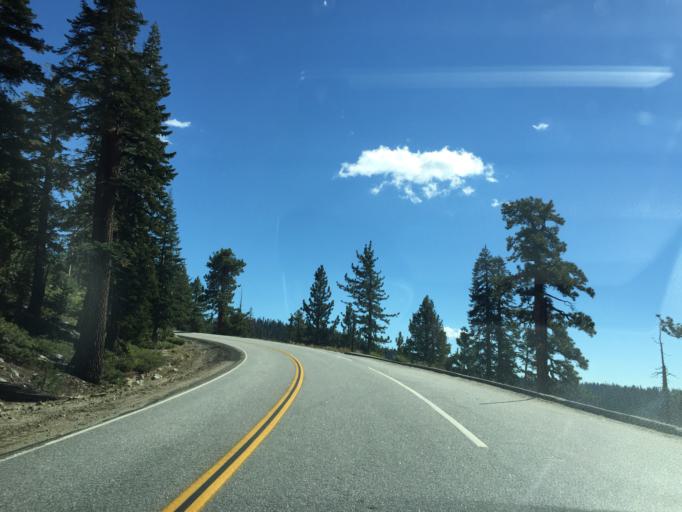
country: US
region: California
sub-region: Mariposa County
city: Yosemite Valley
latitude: 37.8157
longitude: -119.5806
